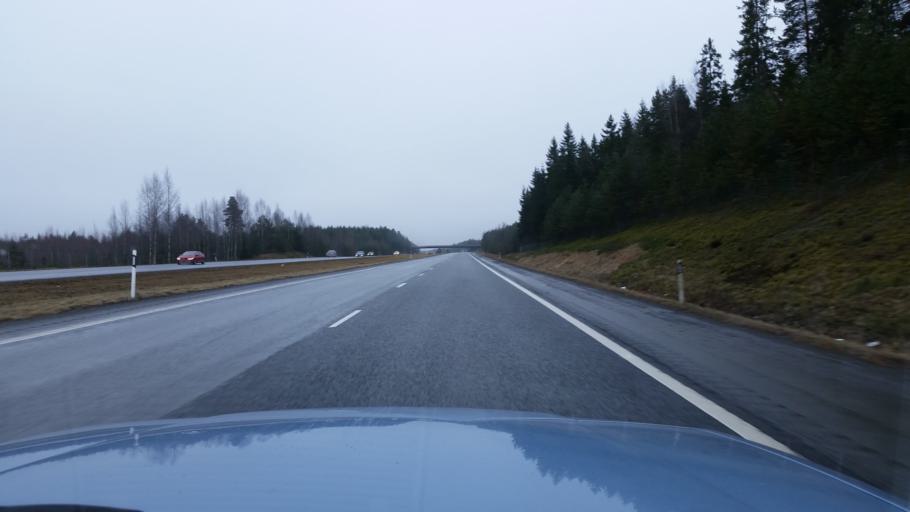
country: FI
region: Haeme
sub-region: Haemeenlinna
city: Kalvola
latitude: 61.1190
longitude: 24.1272
